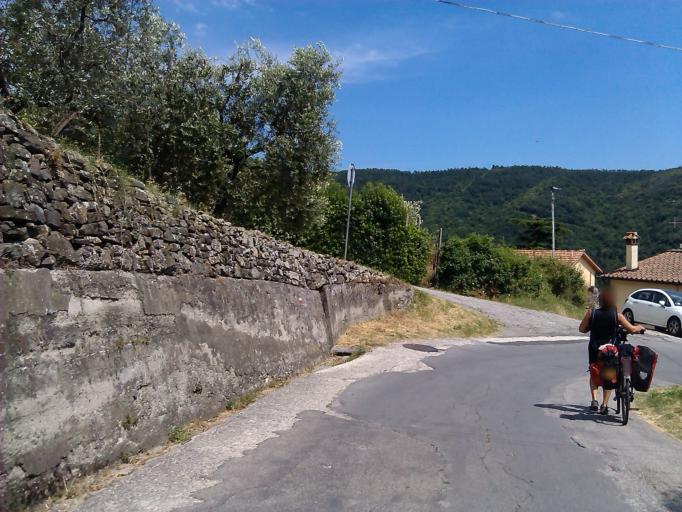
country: IT
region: Tuscany
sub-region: Provincia di Prato
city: Montemurlo
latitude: 43.9627
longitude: 11.0424
